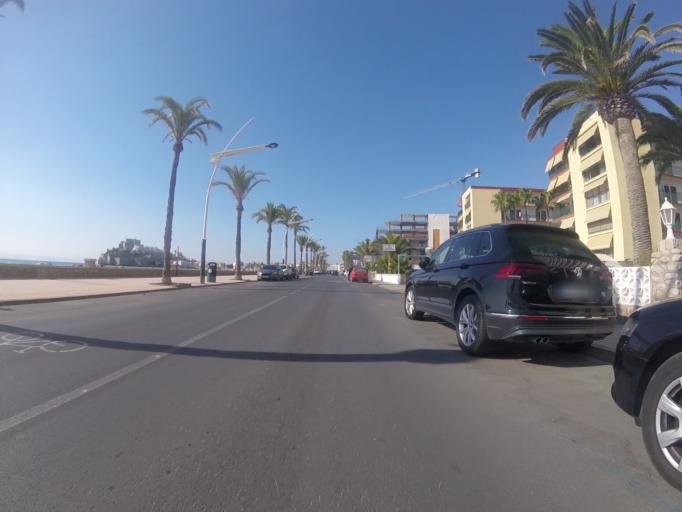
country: ES
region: Valencia
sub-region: Provincia de Castello
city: Peniscola
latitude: 40.3657
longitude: 0.4033
